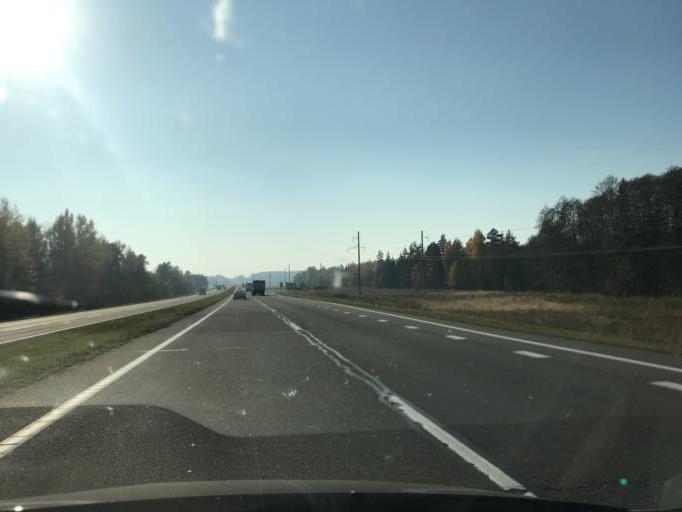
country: BY
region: Minsk
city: Stowbtsy
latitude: 53.5094
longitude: 26.6708
